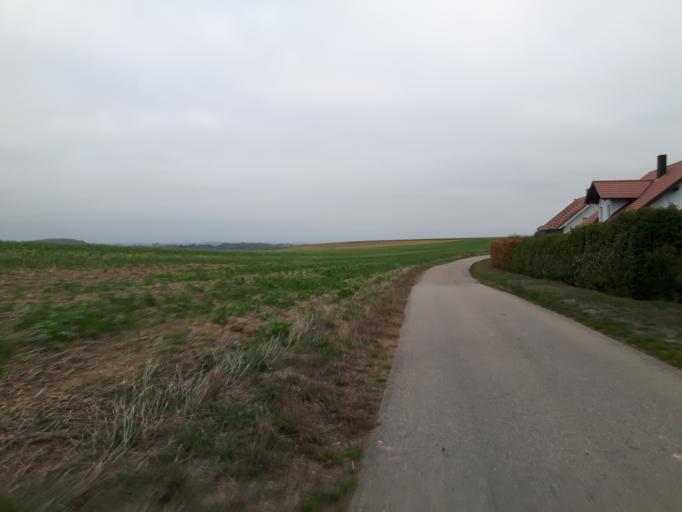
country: DE
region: Baden-Wuerttemberg
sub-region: Karlsruhe Region
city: Sulzfeld
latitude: 49.1730
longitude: 8.8453
